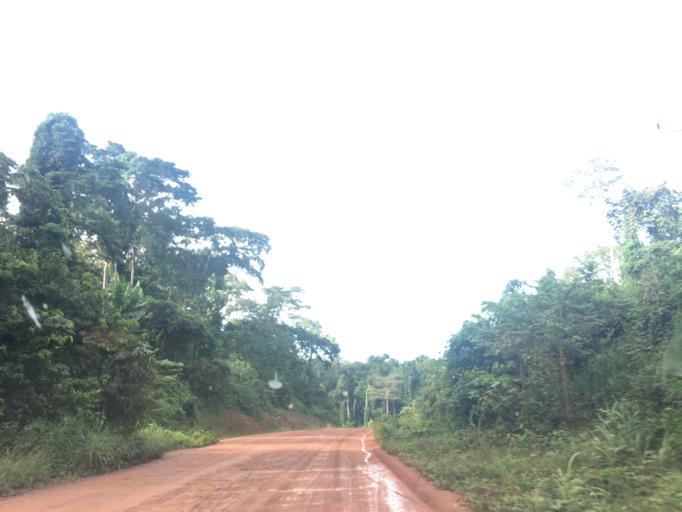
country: GH
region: Western
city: Wassa-Akropong
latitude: 5.9655
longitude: -2.4228
